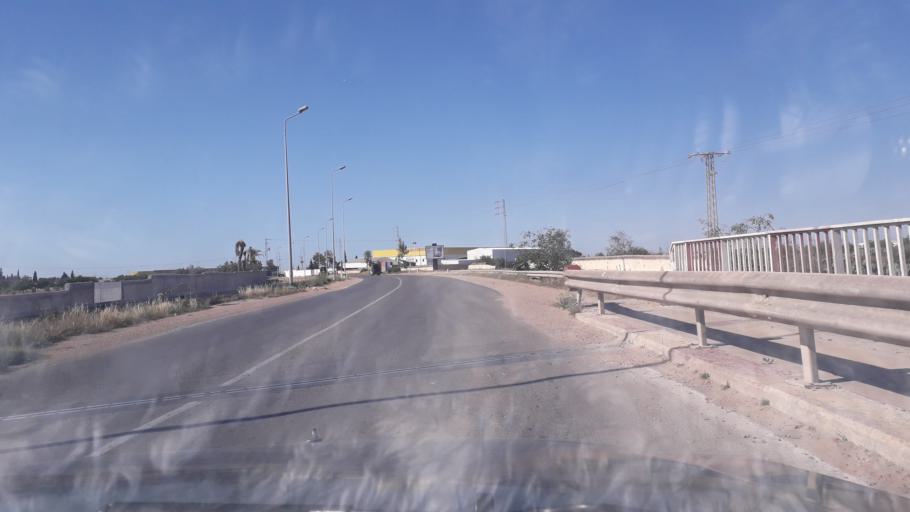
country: TN
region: Safaqis
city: Al Qarmadah
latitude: 34.8756
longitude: 10.7565
